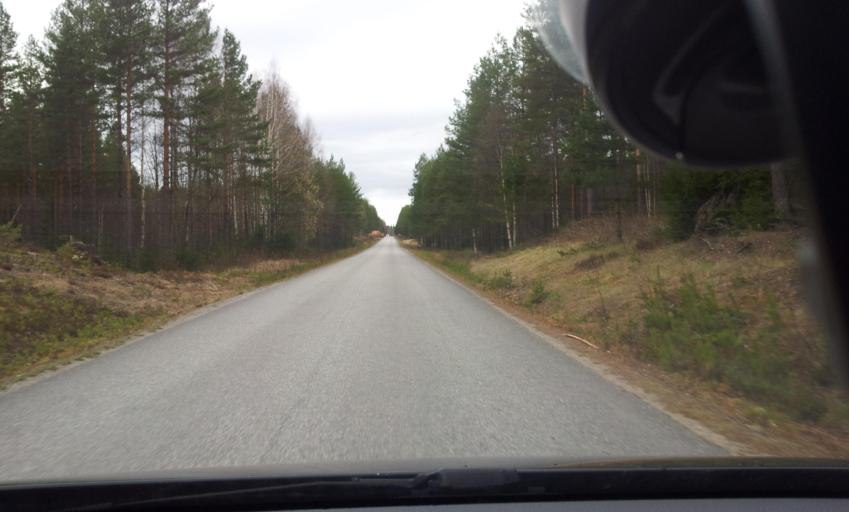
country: SE
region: Gaevleborg
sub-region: Ljusdals Kommun
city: Ljusdal
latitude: 61.8306
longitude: 16.0071
